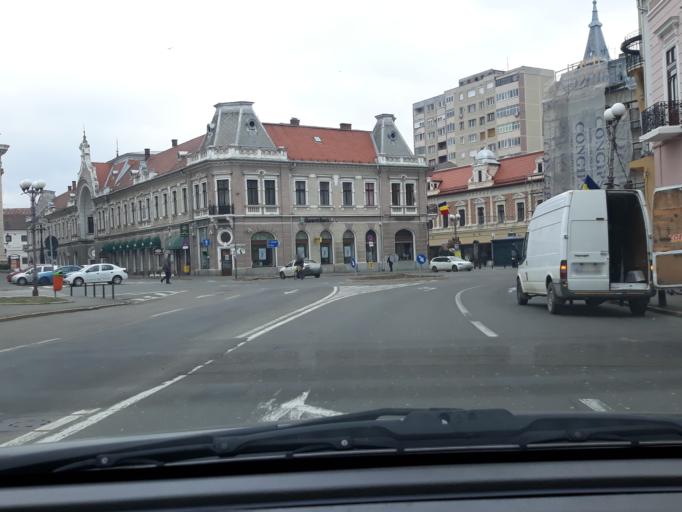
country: RO
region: Bihor
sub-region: Comuna Biharea
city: Oradea
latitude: 47.0566
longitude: 21.9303
